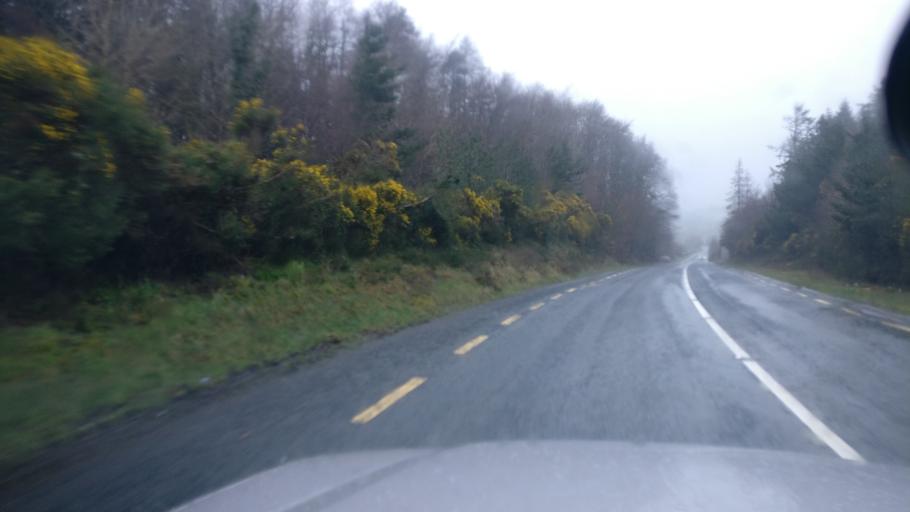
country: IE
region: Connaught
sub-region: County Galway
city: Loughrea
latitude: 53.1443
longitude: -8.4712
